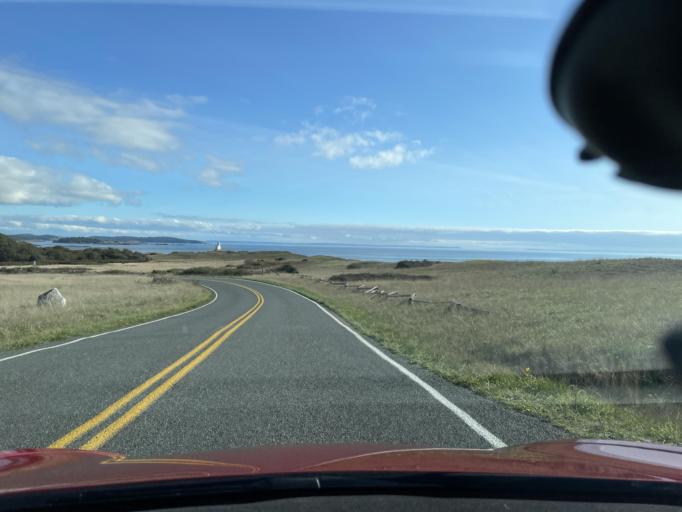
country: US
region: Washington
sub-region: San Juan County
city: Friday Harbor
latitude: 48.4533
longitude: -122.9695
